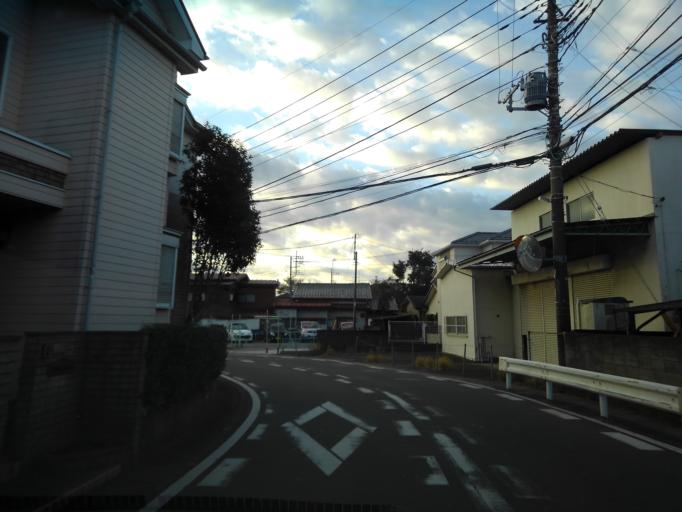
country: JP
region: Saitama
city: Tokorozawa
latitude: 35.7792
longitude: 139.4649
